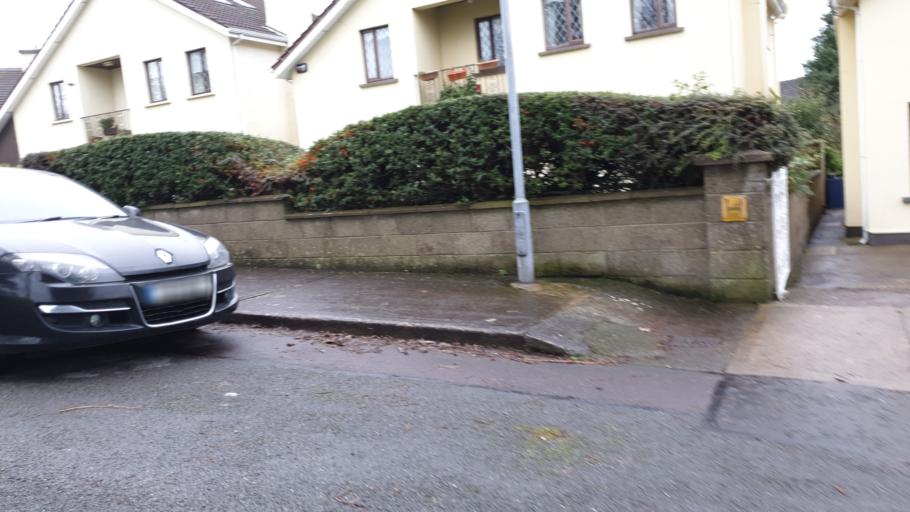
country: IE
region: Munster
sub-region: County Cork
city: Cork
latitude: 51.8884
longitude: -8.4282
